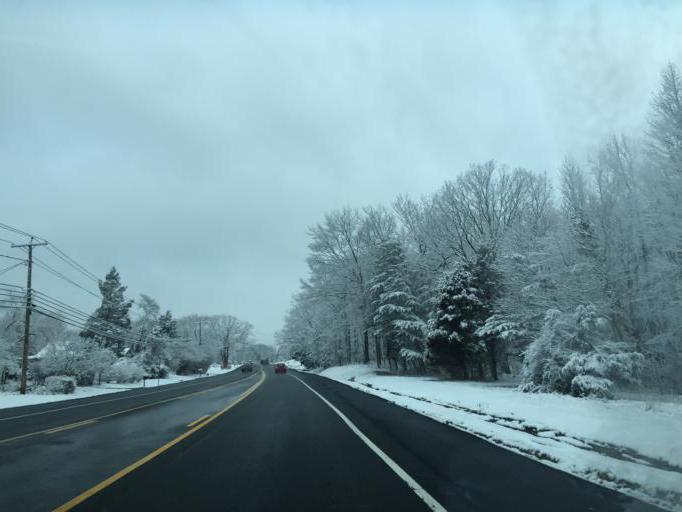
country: US
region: Maryland
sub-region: Harford County
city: Joppatowne
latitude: 39.4522
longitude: -76.3555
